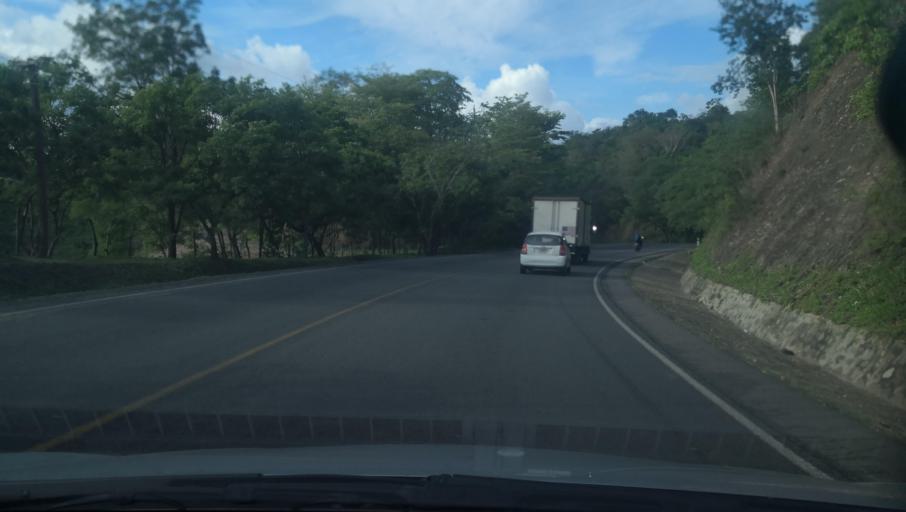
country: NI
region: Nueva Segovia
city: Ocotal
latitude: 13.5965
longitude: -86.4724
